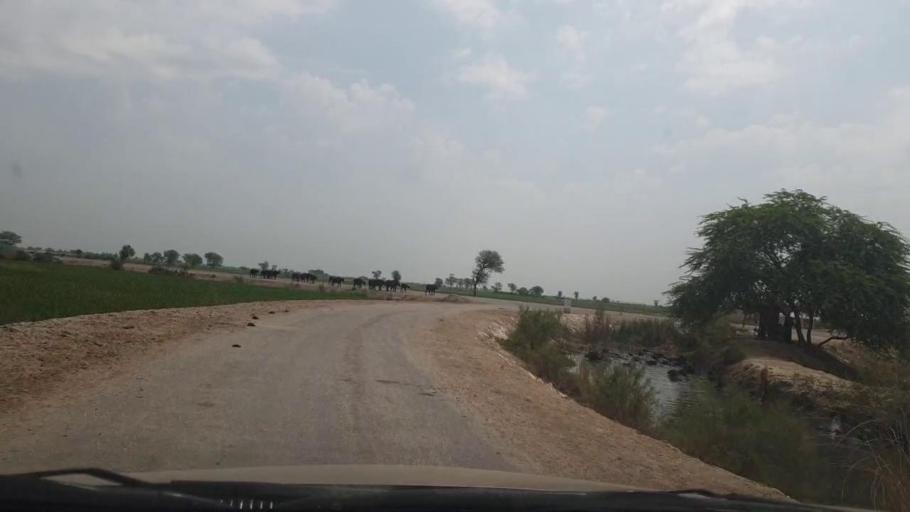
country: PK
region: Sindh
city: Ratodero
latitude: 27.7096
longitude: 68.2739
